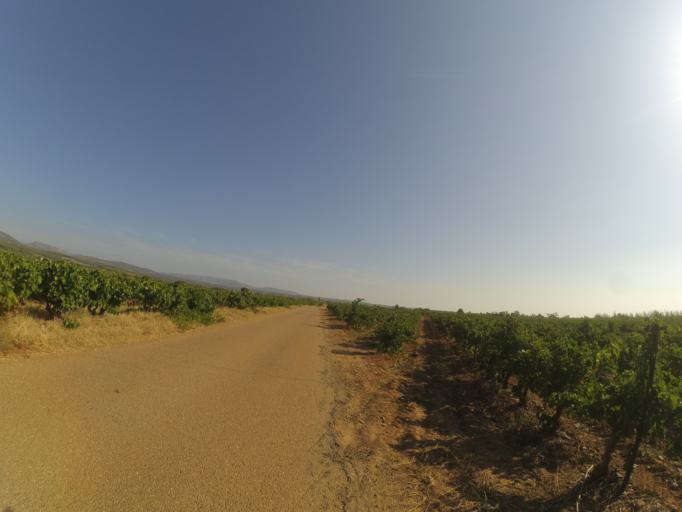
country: FR
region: Languedoc-Roussillon
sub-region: Departement des Pyrenees-Orientales
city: Rivesaltes
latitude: 42.7900
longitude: 2.8464
